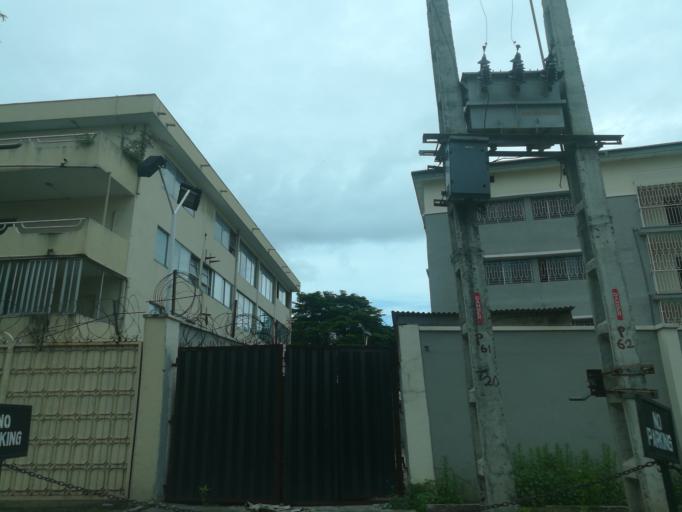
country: NG
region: Lagos
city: Ikoyi
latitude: 6.4353
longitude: 3.4211
